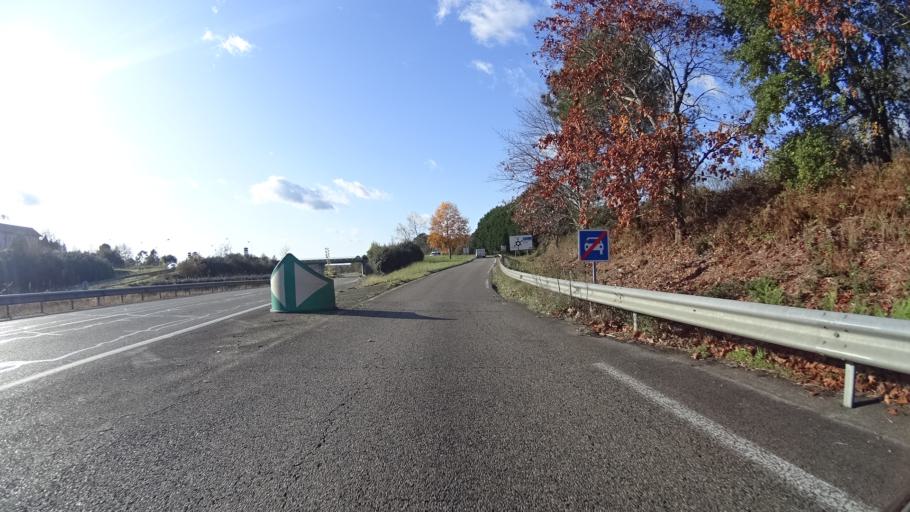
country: FR
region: Aquitaine
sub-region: Departement des Landes
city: Saint-Paul-les-Dax
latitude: 43.7448
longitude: -1.0532
